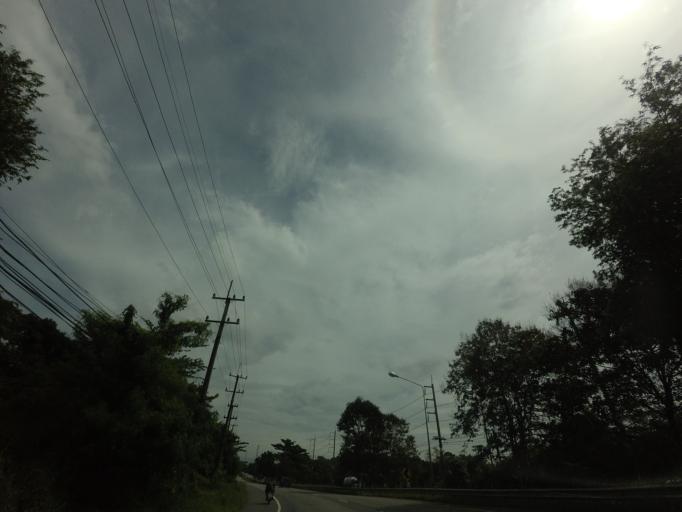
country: TH
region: Rayong
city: Klaeng
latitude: 12.7134
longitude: 101.5635
